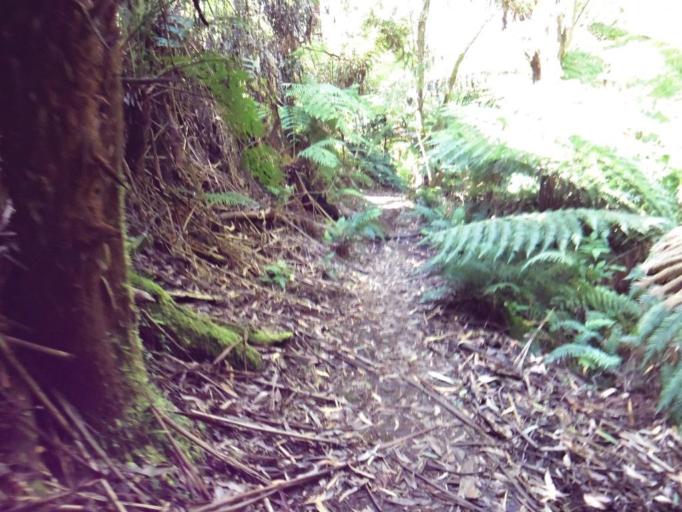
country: AU
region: Victoria
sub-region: Yarra Ranges
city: Mount Dandenong
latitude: -37.8333
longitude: 145.3659
